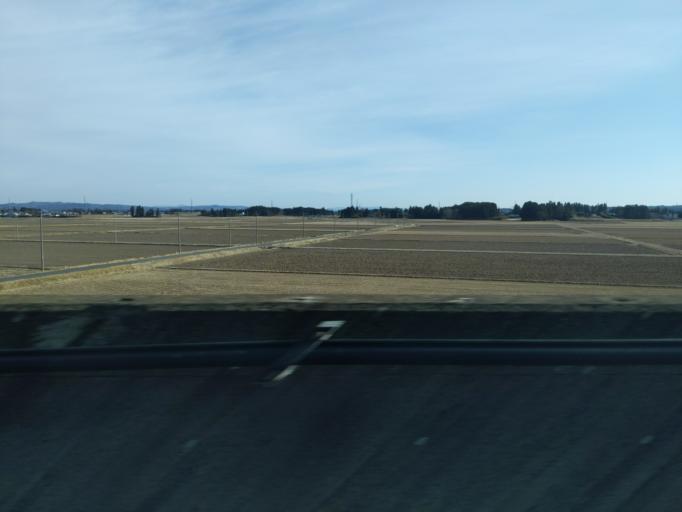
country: JP
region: Miyagi
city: Furukawa
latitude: 38.5457
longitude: 140.9617
